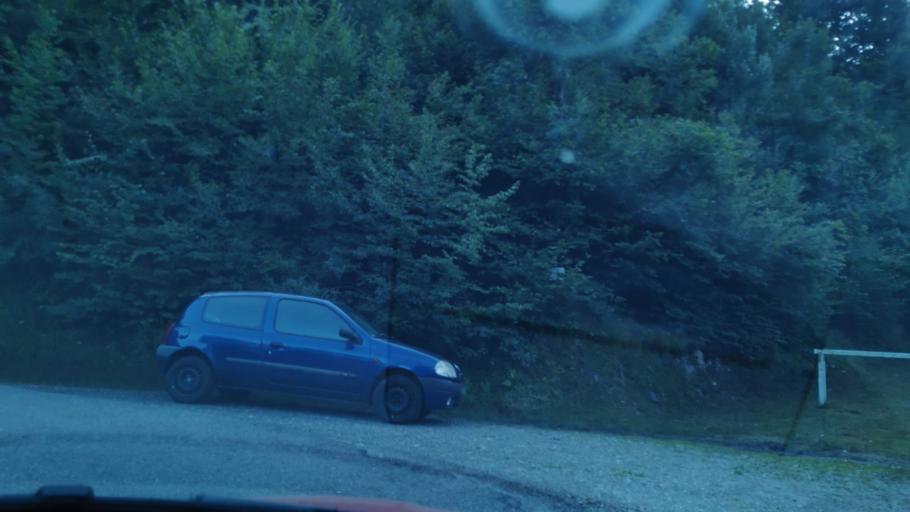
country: IT
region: Lombardy
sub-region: Provincia di Lecco
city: Moggio
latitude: 45.9108
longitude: 9.4949
